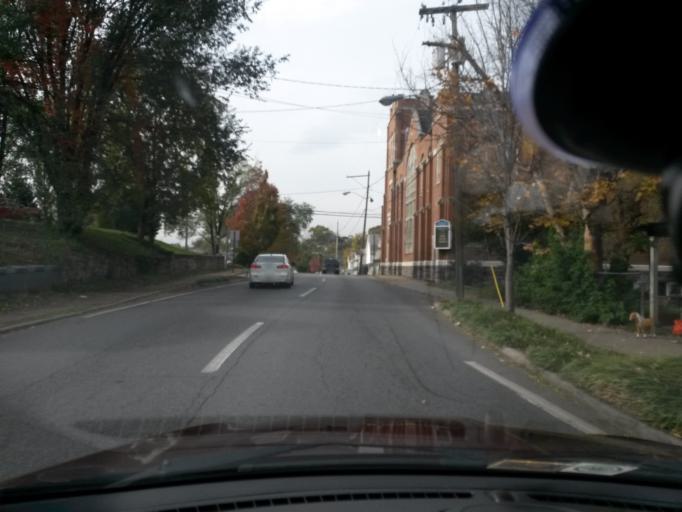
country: US
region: Virginia
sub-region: City of Roanoke
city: Cedar Bluff
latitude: 37.2690
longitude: -79.9296
